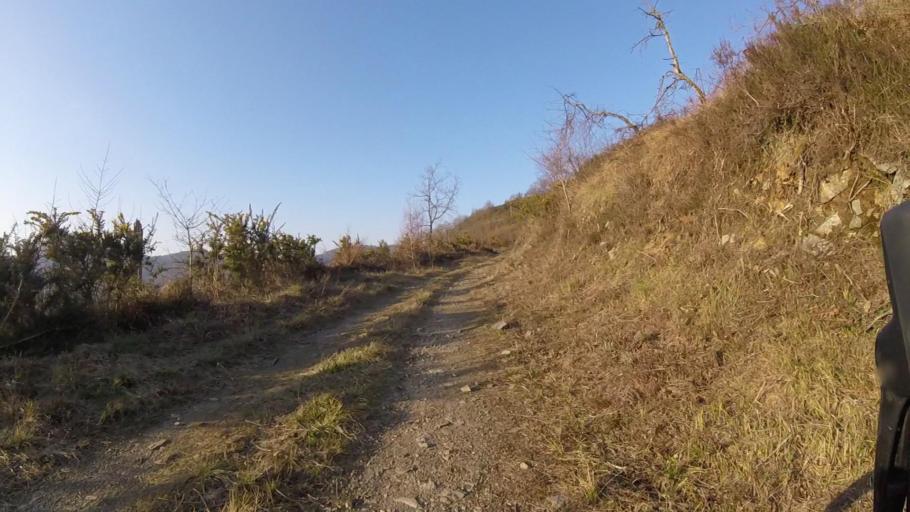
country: ES
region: Navarre
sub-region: Provincia de Navarra
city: Arano
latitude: 43.2221
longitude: -1.8605
